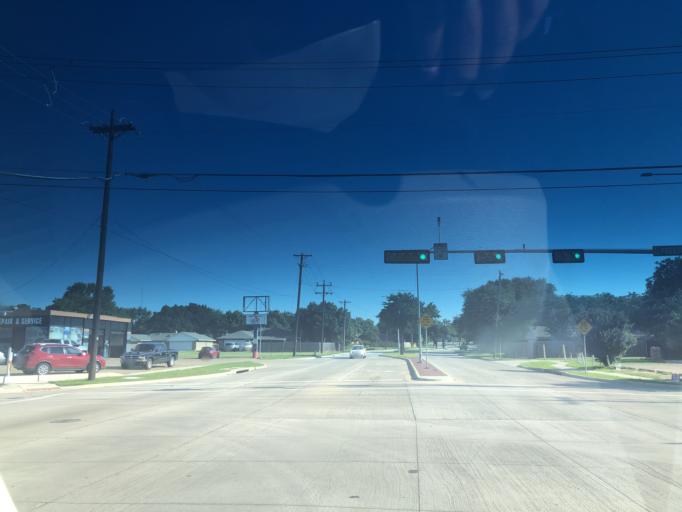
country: US
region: Texas
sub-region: Dallas County
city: Grand Prairie
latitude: 32.7133
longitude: -97.0153
